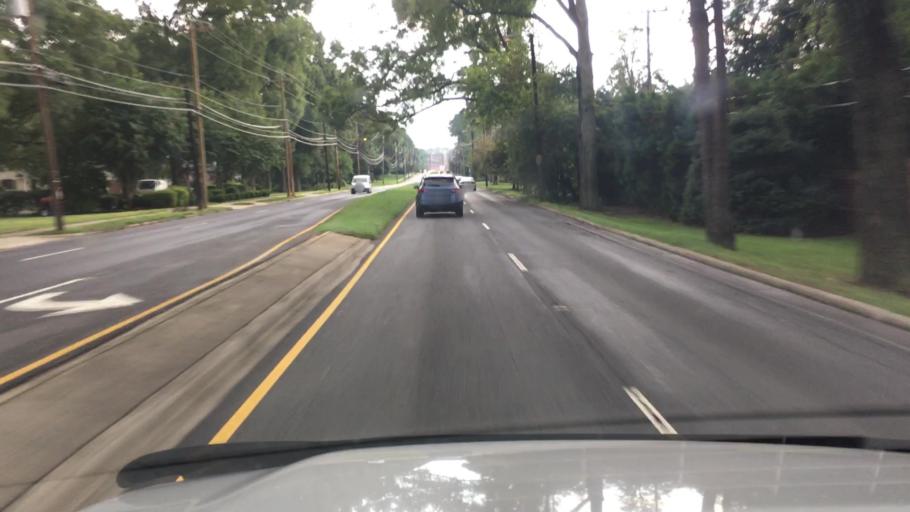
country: US
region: North Carolina
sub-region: Mecklenburg County
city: Charlotte
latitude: 35.1665
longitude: -80.8036
